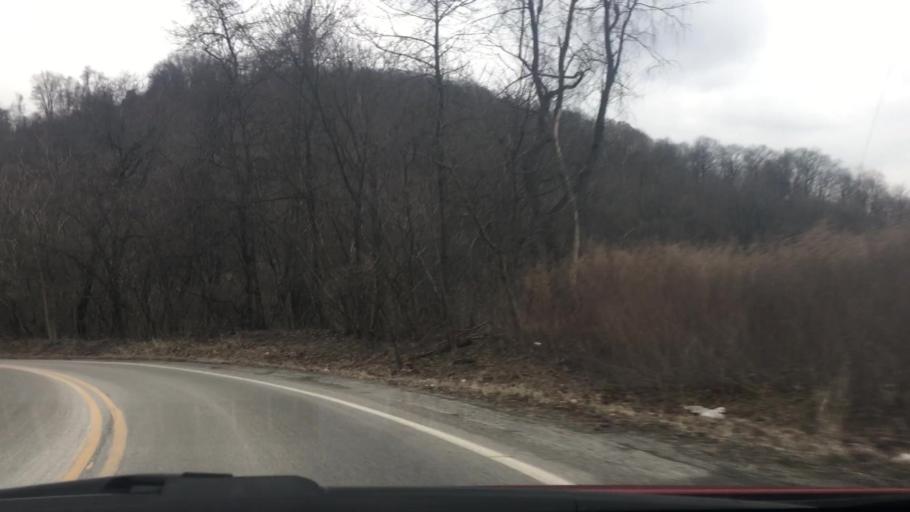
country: US
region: Pennsylvania
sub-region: Allegheny County
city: Lincoln
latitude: 40.3020
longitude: -79.8644
